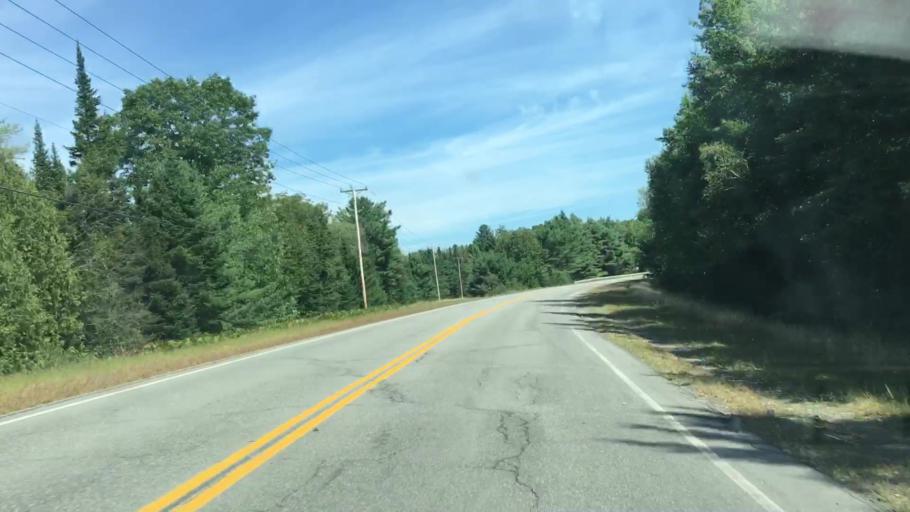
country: US
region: Maine
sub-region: Piscataquis County
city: Milo
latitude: 45.2299
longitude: -68.9414
